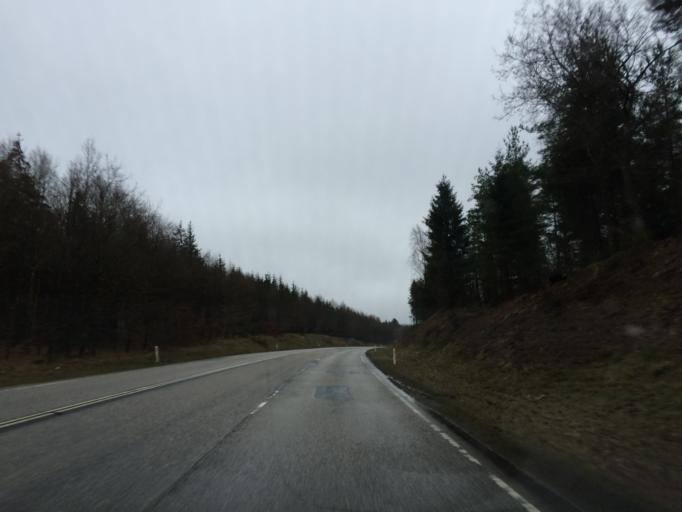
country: DK
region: North Denmark
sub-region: Mariagerfjord Kommune
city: Arden
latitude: 56.8192
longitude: 9.8193
